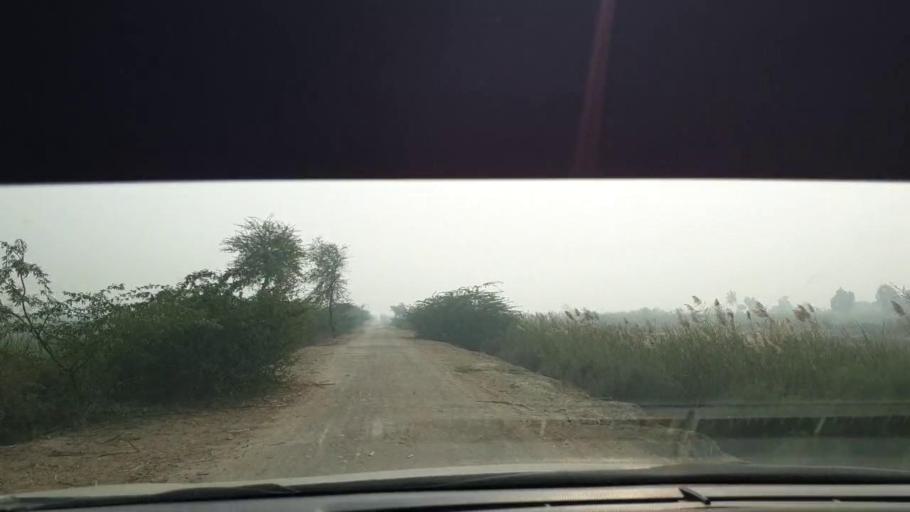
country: PK
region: Sindh
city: Berani
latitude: 25.8371
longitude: 68.8349
